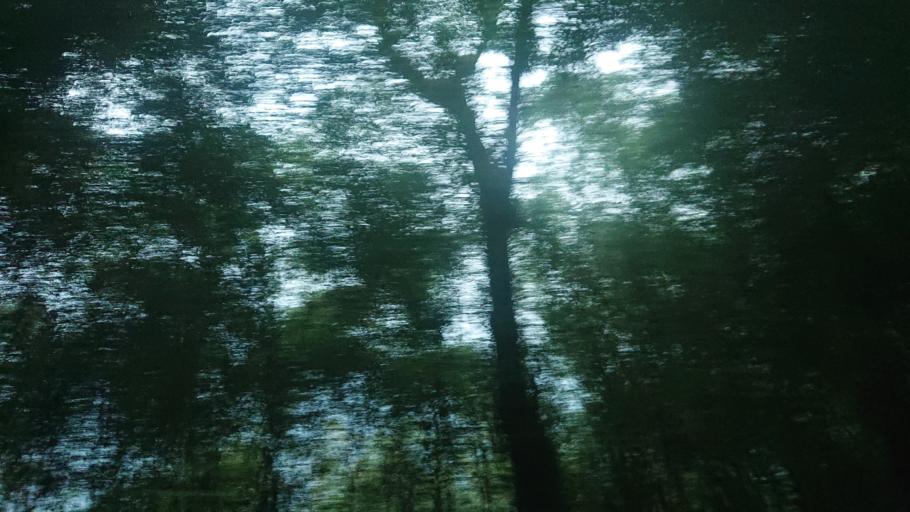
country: TW
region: Taiwan
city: Lugu
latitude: 23.5853
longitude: 120.7250
